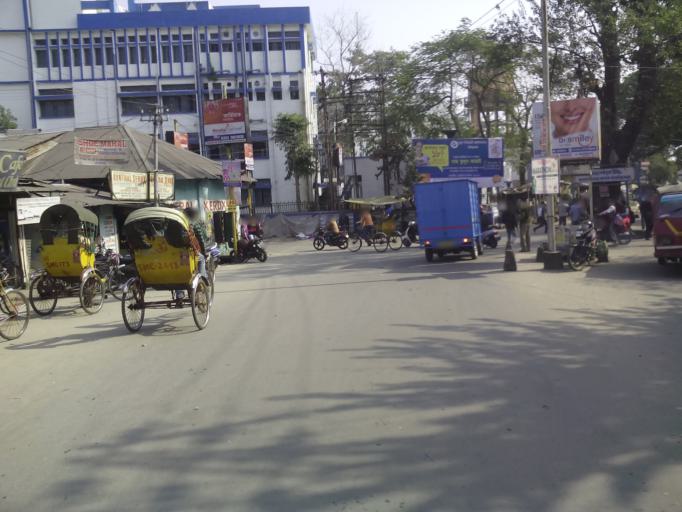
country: IN
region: West Bengal
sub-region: Darjiling
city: Shiliguri
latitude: 26.7110
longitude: 88.4272
